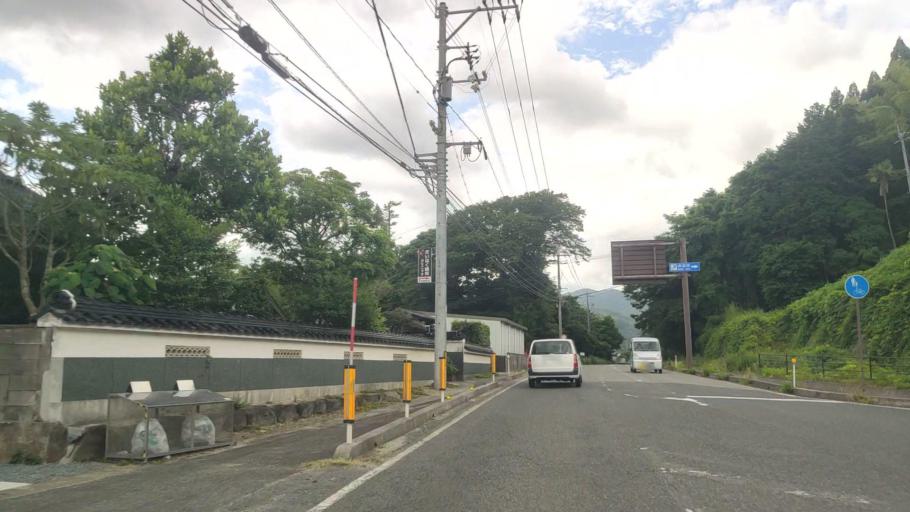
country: JP
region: Tottori
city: Yonago
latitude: 35.3403
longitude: 133.4340
